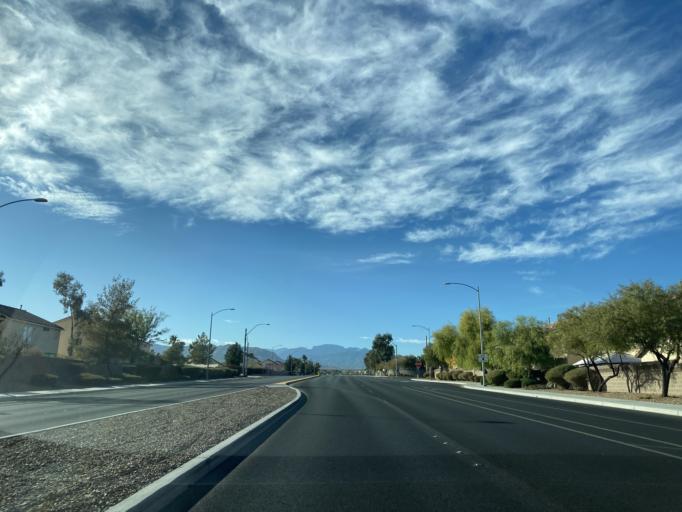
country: US
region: Nevada
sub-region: Clark County
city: Summerlin South
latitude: 36.3066
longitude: -115.2861
